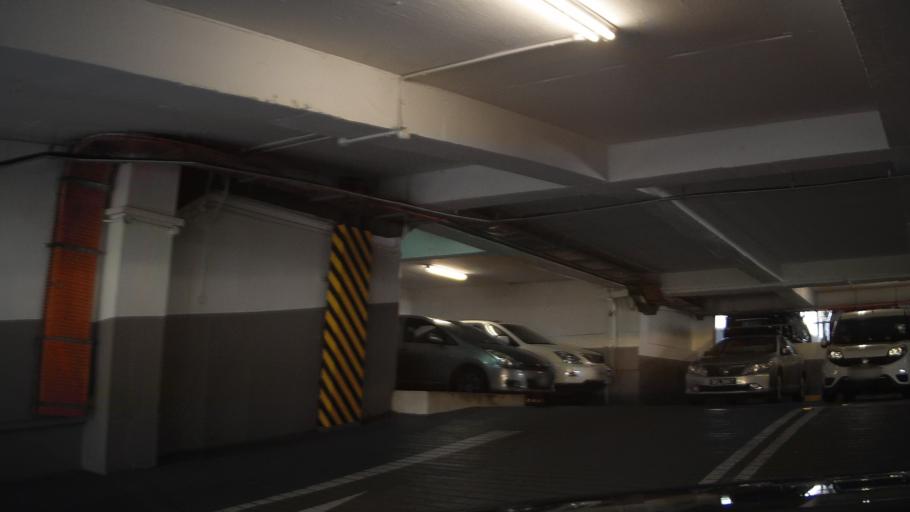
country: SG
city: Singapore
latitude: 1.2698
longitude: 103.8409
